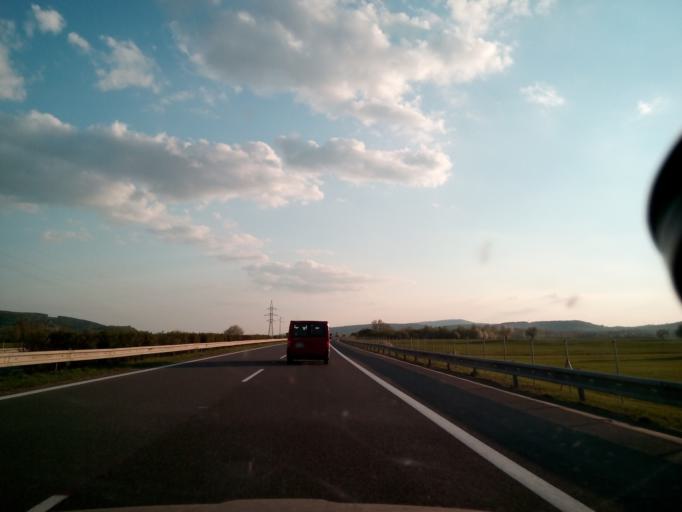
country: SK
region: Trenciansky
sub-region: Okres Trencin
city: Trencin
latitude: 48.8369
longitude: 17.9348
